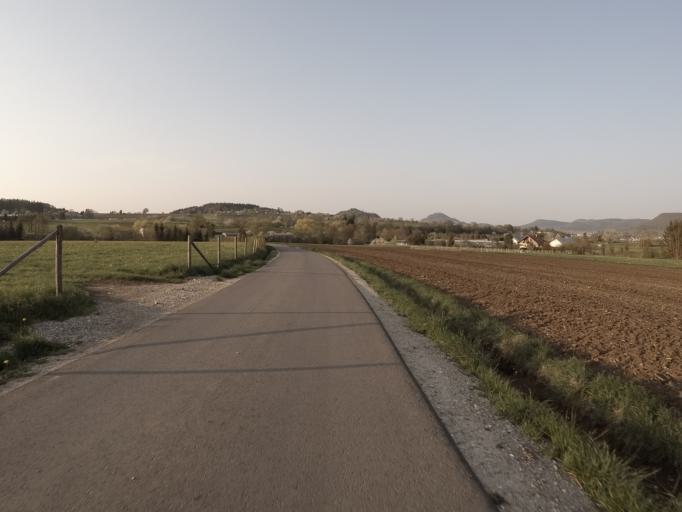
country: DE
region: Baden-Wuerttemberg
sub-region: Tuebingen Region
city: Pfullingen
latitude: 48.4495
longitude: 9.1978
